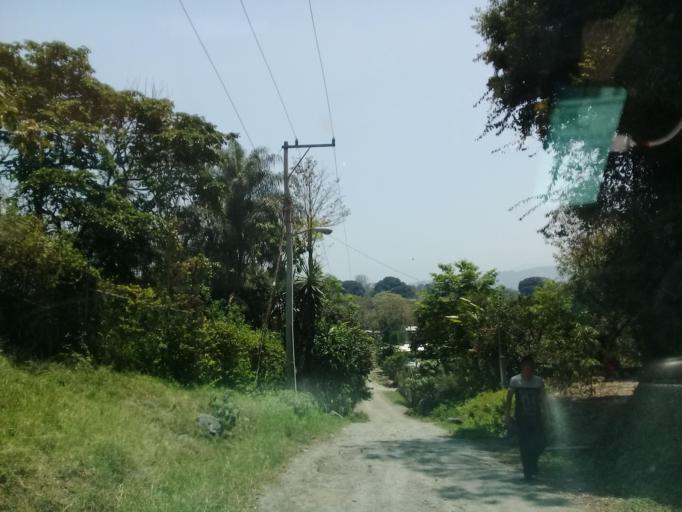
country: MX
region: Veracruz
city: Paraje Nuevo
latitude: 18.8730
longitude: -96.8653
